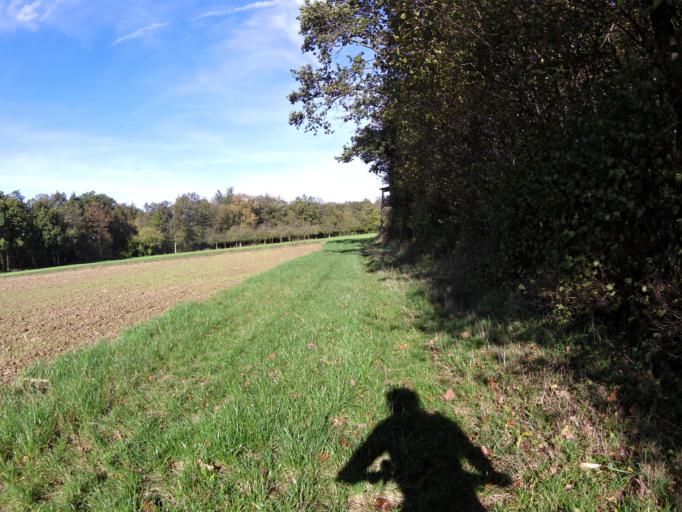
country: DE
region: Bavaria
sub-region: Regierungsbezirk Unterfranken
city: Sulzfeld am Main
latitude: 49.7132
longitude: 10.0938
